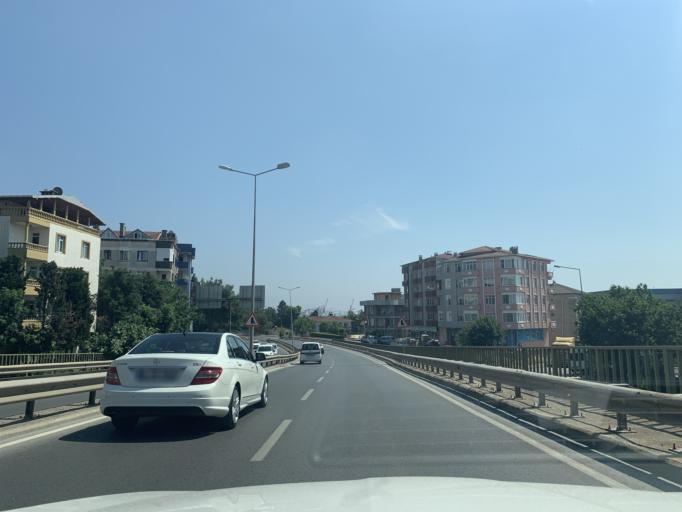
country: TR
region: Istanbul
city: Pendik
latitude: 40.8599
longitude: 29.2732
